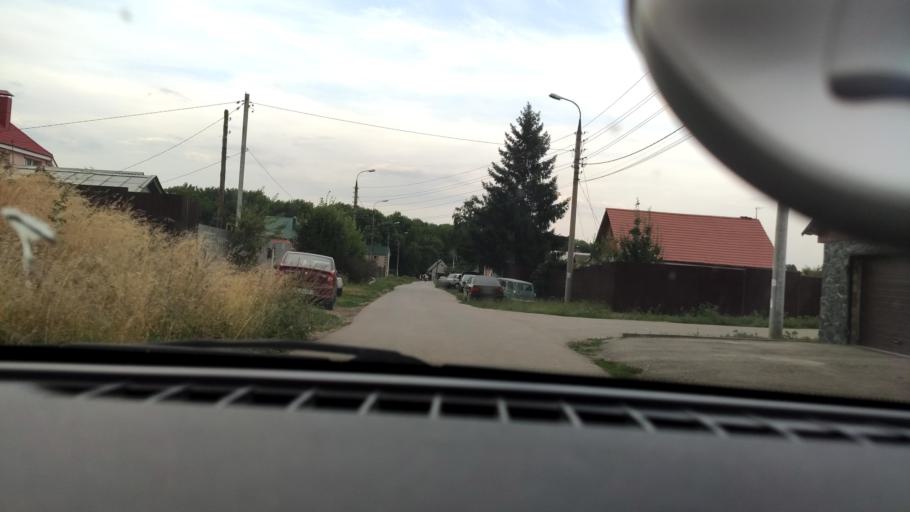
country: RU
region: Samara
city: Petra-Dubrava
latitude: 53.2953
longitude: 50.3724
